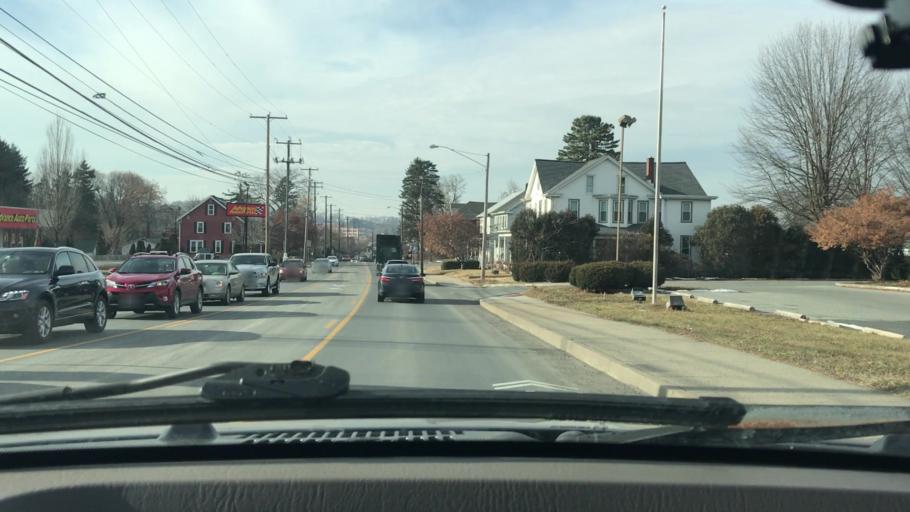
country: US
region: Pennsylvania
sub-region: Lancaster County
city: Elizabethtown
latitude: 40.1436
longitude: -76.5971
